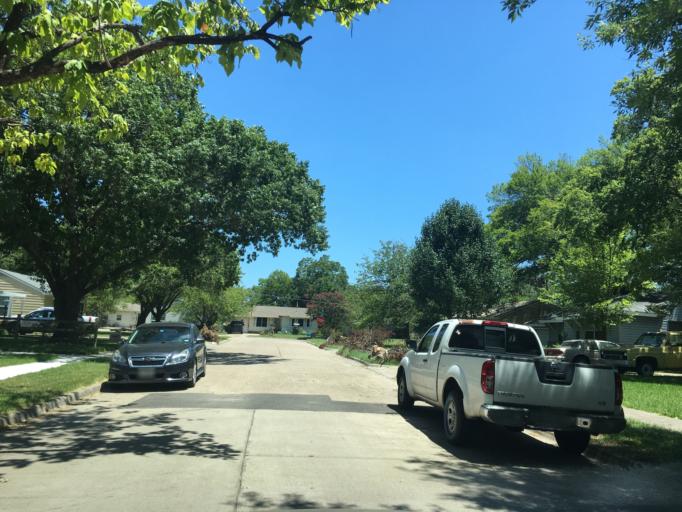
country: US
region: Texas
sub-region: Dallas County
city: Garland
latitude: 32.8434
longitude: -96.6772
